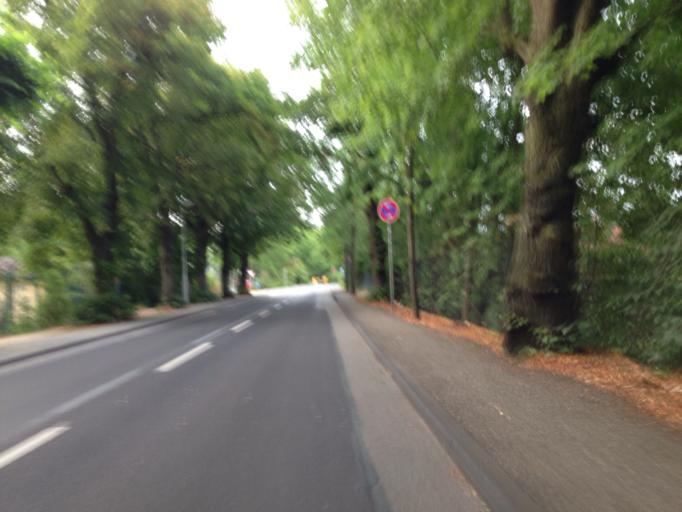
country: DE
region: Hesse
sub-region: Regierungsbezirk Giessen
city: Giessen
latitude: 50.5792
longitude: 8.6598
